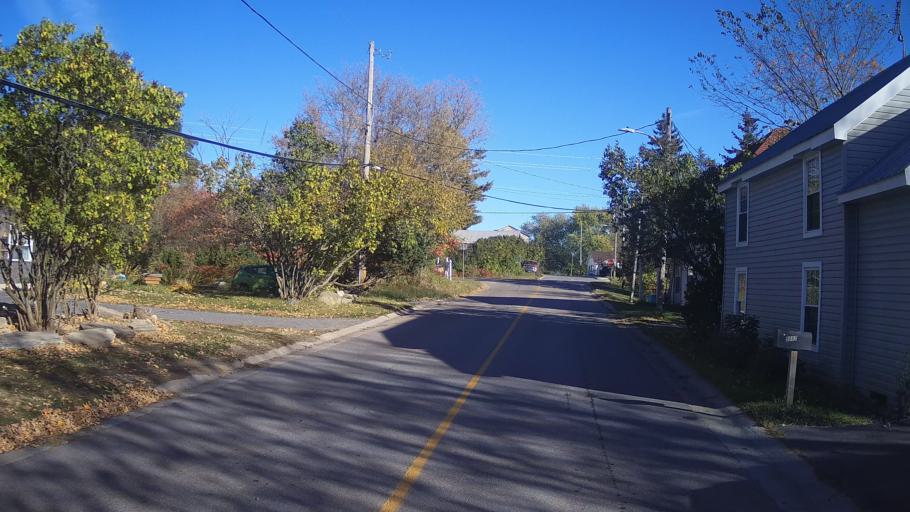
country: CA
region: Ontario
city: Kingston
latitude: 44.4662
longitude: -76.4930
